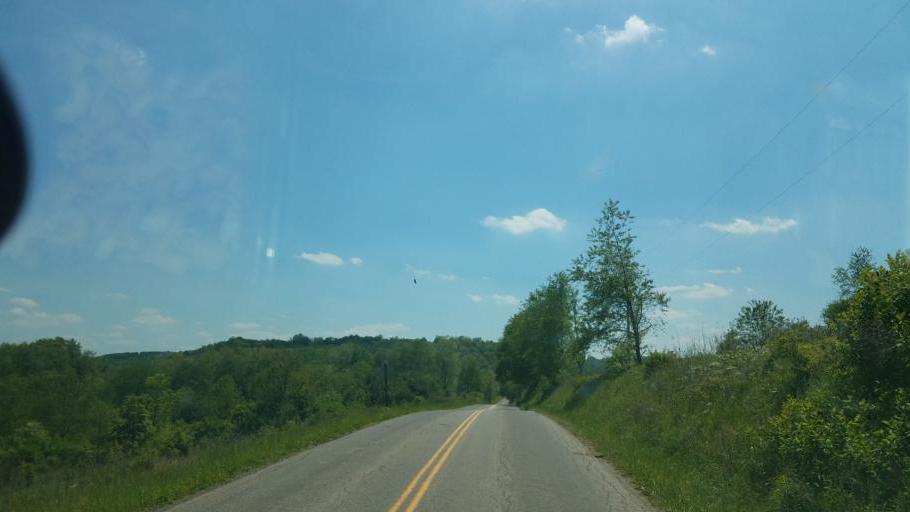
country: US
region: Ohio
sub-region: Knox County
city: Oak Hill
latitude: 40.2609
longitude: -82.2841
